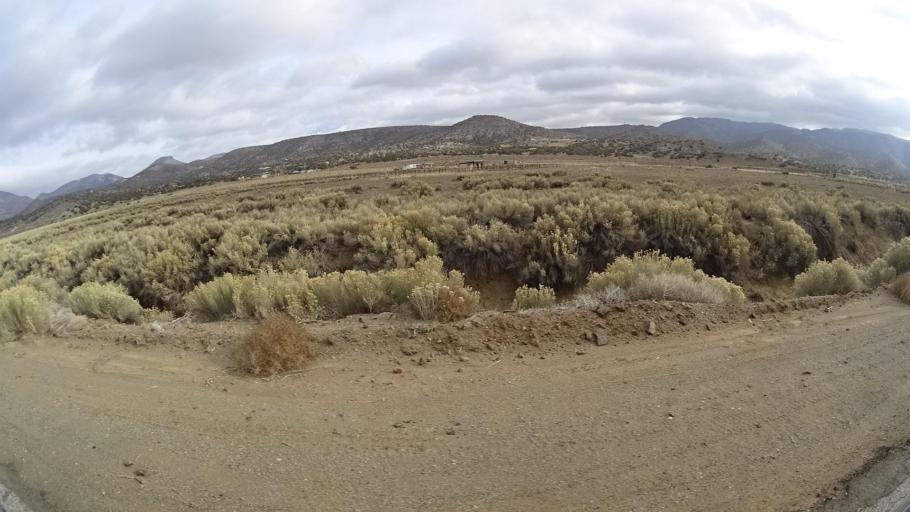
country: US
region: California
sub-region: Kern County
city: Tehachapi
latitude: 35.1640
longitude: -118.3301
